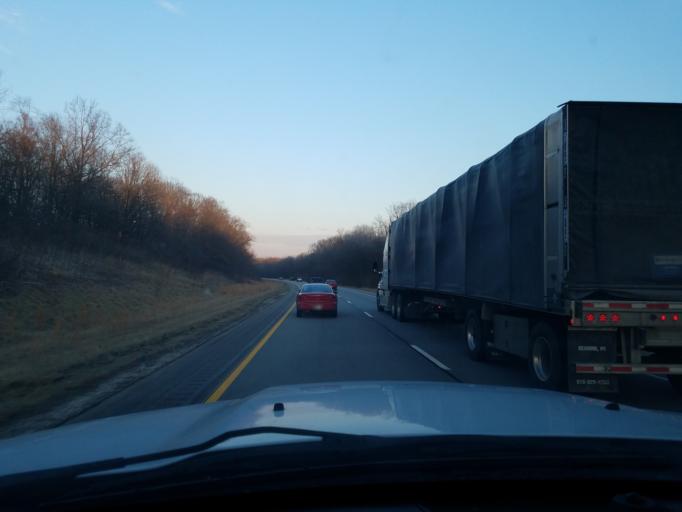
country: US
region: Indiana
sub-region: Warrick County
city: Chandler
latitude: 38.1699
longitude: -87.4305
